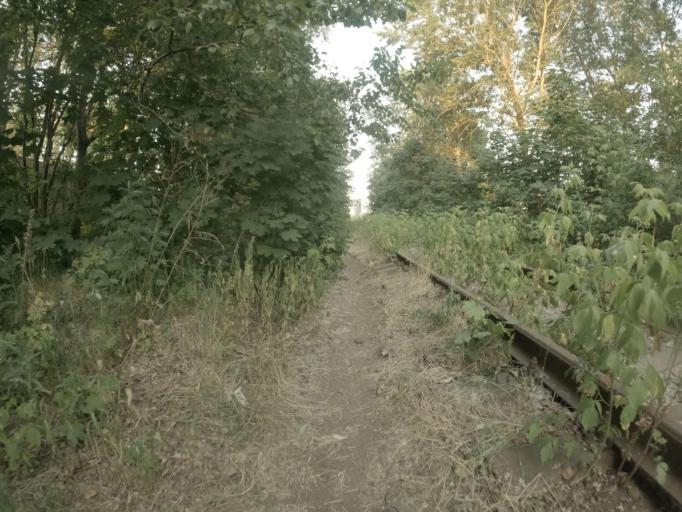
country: RU
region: St.-Petersburg
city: Krasnogvargeisky
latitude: 59.9410
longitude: 30.4390
